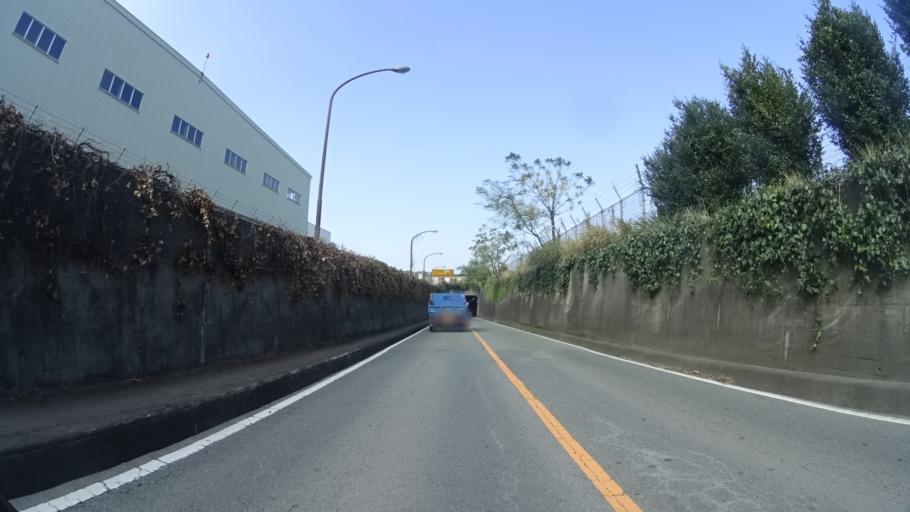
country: JP
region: Kumamoto
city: Ozu
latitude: 32.8339
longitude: 130.8558
